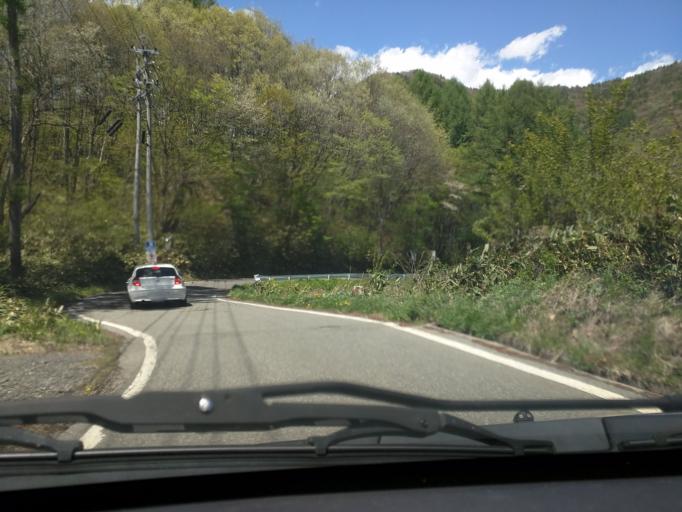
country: JP
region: Nagano
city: Nagano-shi
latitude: 36.6847
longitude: 138.1148
